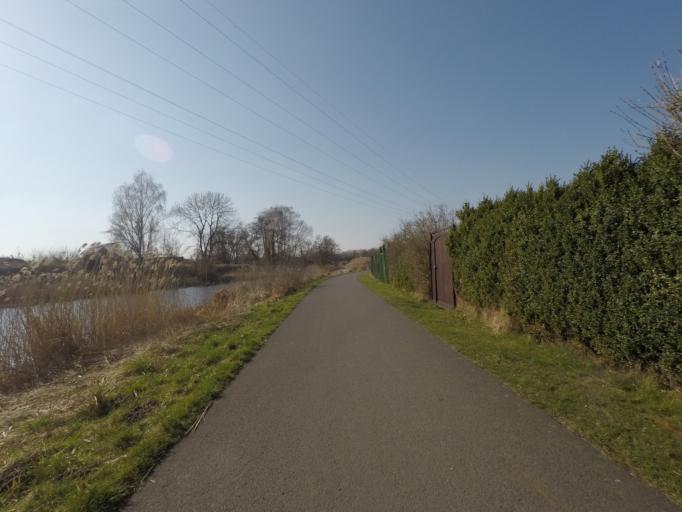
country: DE
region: Brandenburg
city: Eberswalde
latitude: 52.8373
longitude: 13.8081
